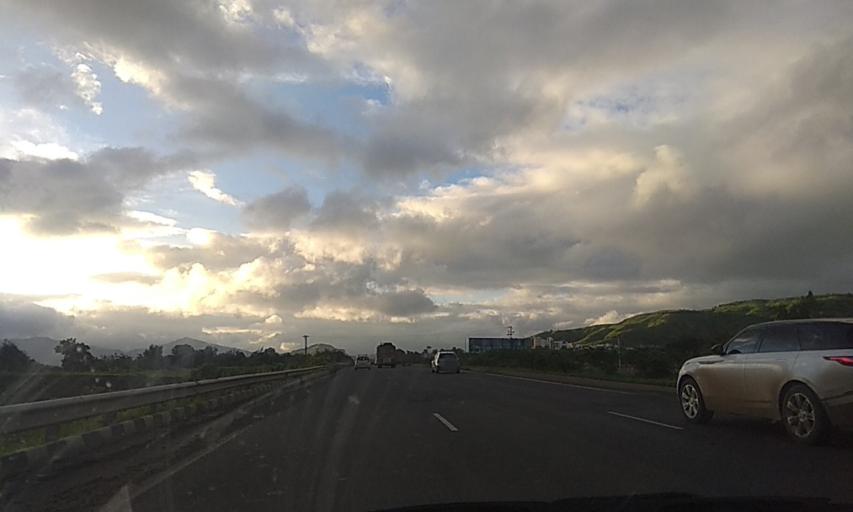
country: IN
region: Maharashtra
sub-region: Satara Division
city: Satara
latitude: 17.7337
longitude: 74.0139
